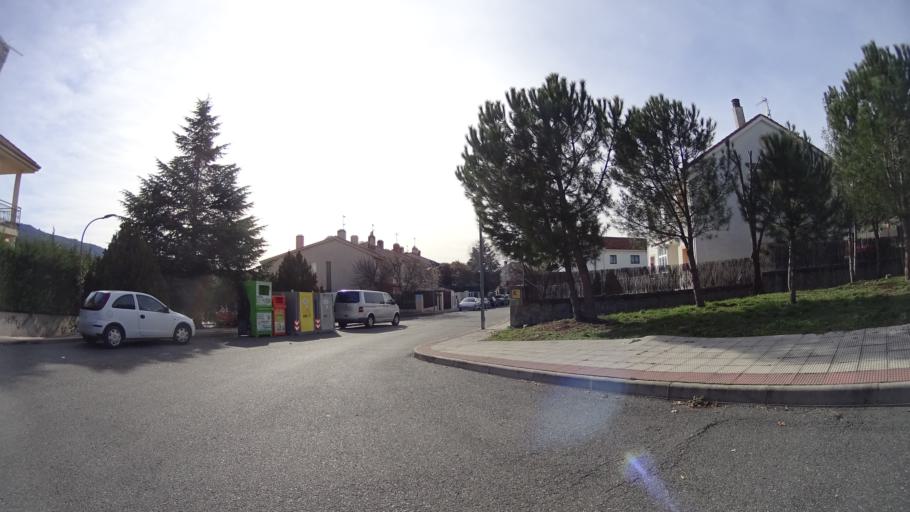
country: ES
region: Madrid
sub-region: Provincia de Madrid
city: Moralzarzal
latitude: 40.6778
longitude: -3.9746
